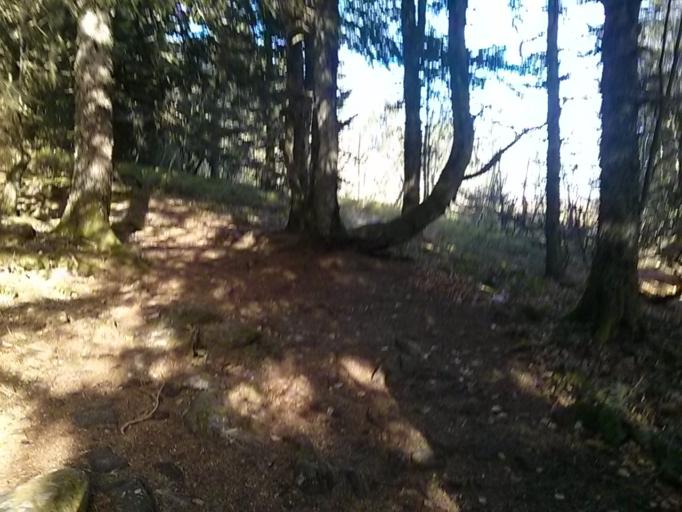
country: FR
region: Rhone-Alpes
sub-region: Departement de la Loire
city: Saint-Julien-Molin-Molette
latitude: 45.3830
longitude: 4.5860
